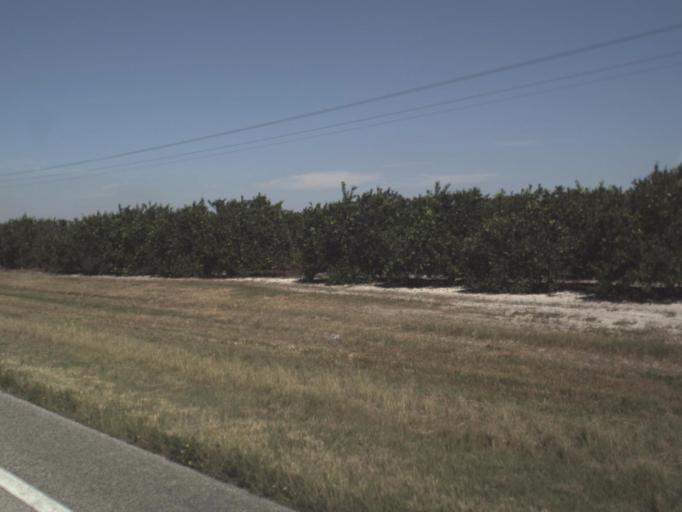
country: US
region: Florida
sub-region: Highlands County
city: Placid Lakes
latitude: 27.2040
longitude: -81.3286
